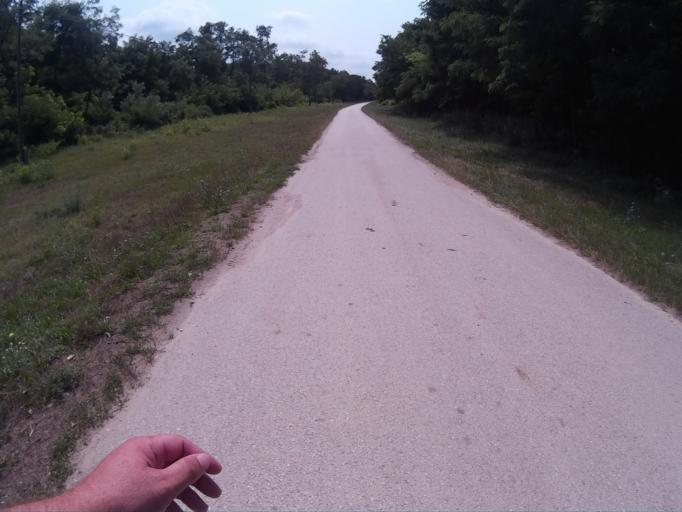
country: HU
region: Veszprem
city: Papa
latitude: 47.2945
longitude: 17.5980
